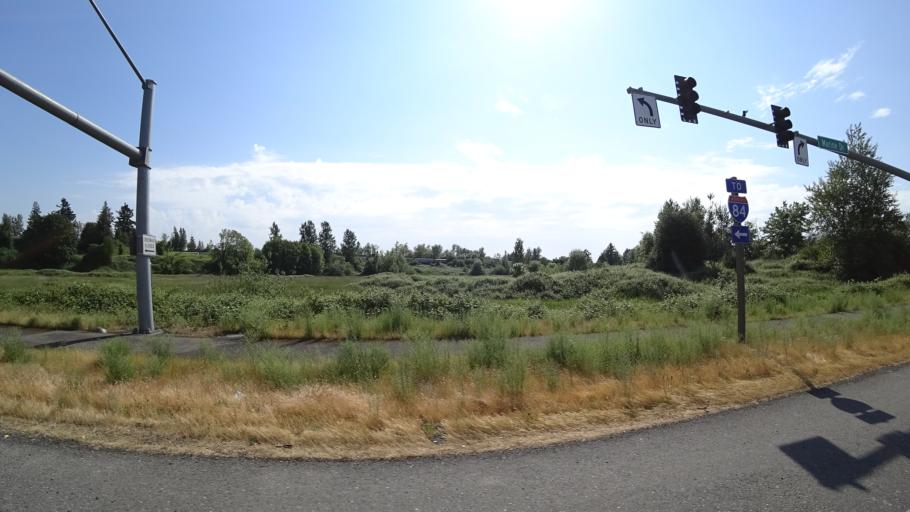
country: US
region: Oregon
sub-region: Multnomah County
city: Wood Village
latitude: 45.5494
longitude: -122.4182
